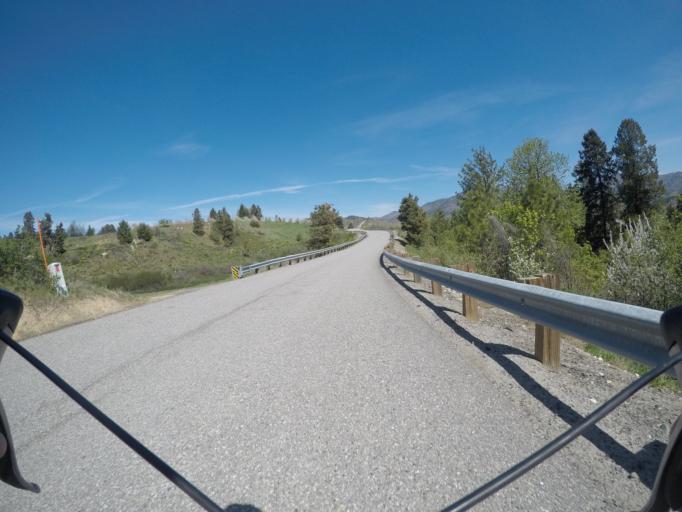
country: US
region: Washington
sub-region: Chelan County
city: Leavenworth
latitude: 47.5442
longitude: -120.5797
